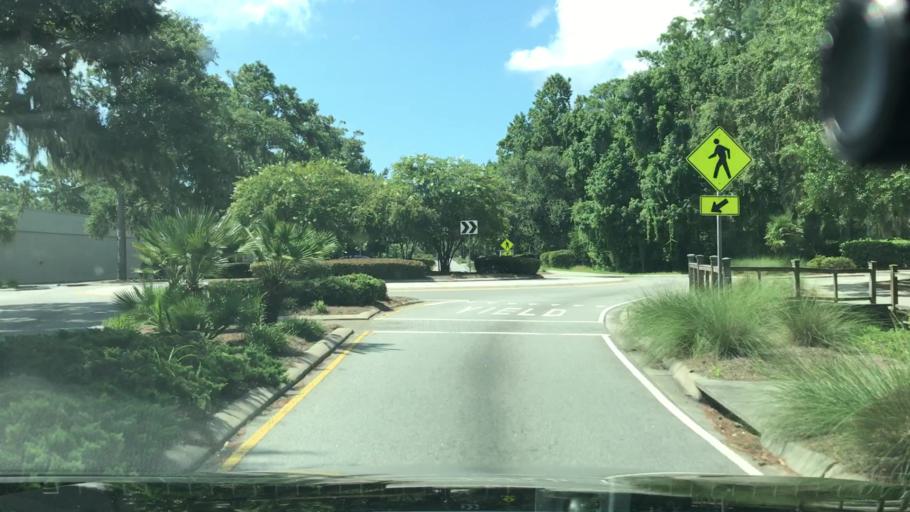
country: US
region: South Carolina
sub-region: Beaufort County
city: Hilton Head Island
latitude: 32.2126
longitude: -80.7027
